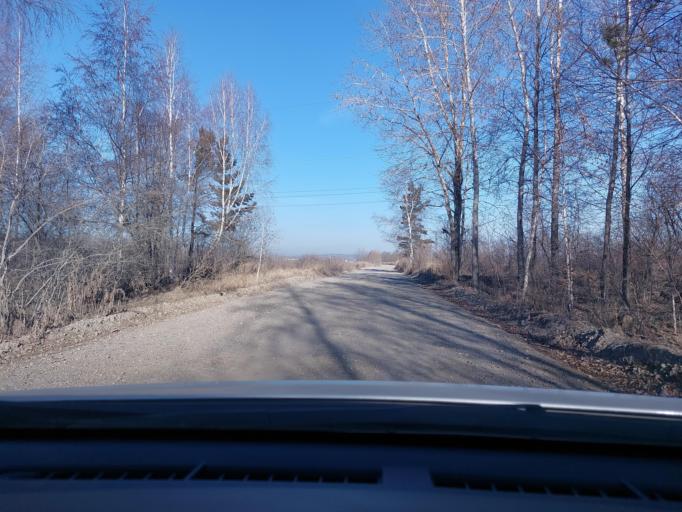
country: RU
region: Irkutsk
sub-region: Irkutskiy Rayon
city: Irkutsk
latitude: 52.3020
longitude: 104.2761
